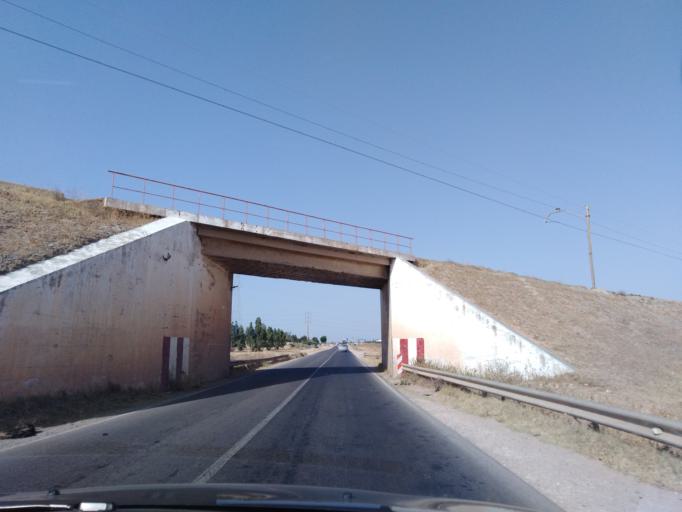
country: MA
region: Doukkala-Abda
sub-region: Safi
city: Safi
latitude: 32.2629
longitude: -8.9565
